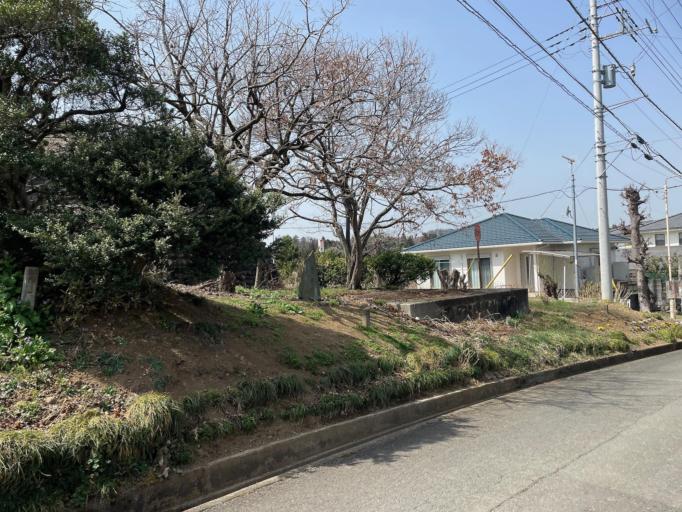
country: JP
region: Saitama
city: Ogawa
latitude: 36.0834
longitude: 139.2859
